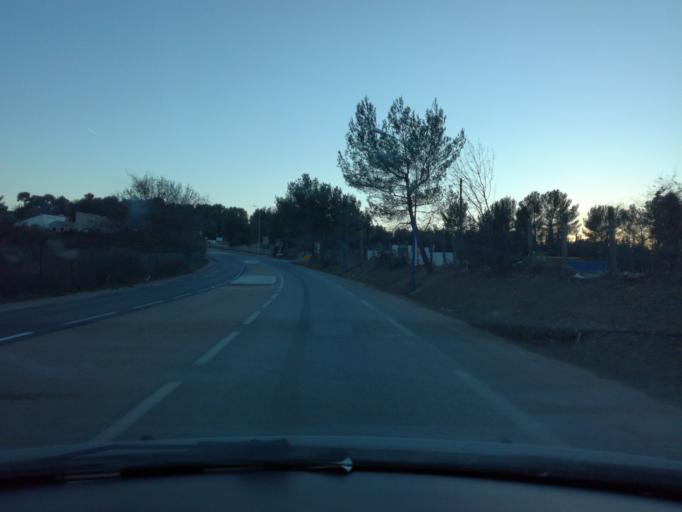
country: FR
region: Provence-Alpes-Cote d'Azur
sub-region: Departement des Bouches-du-Rhone
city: Allauch
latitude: 43.3223
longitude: 5.4693
